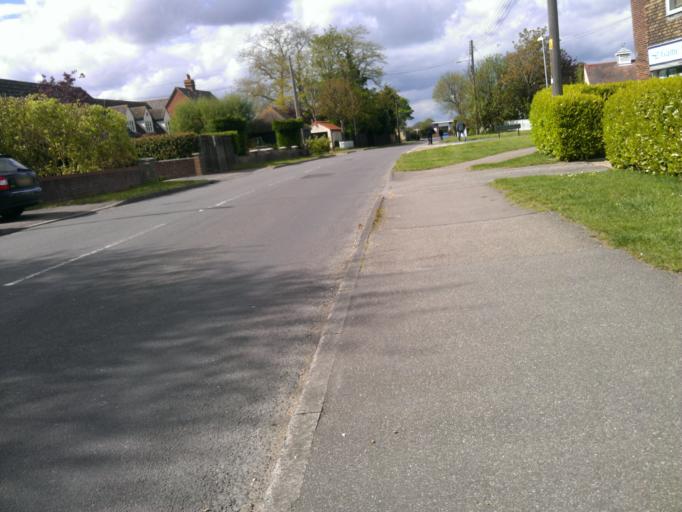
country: GB
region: England
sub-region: Essex
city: Eight Ash Green
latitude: 51.8788
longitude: 0.7970
